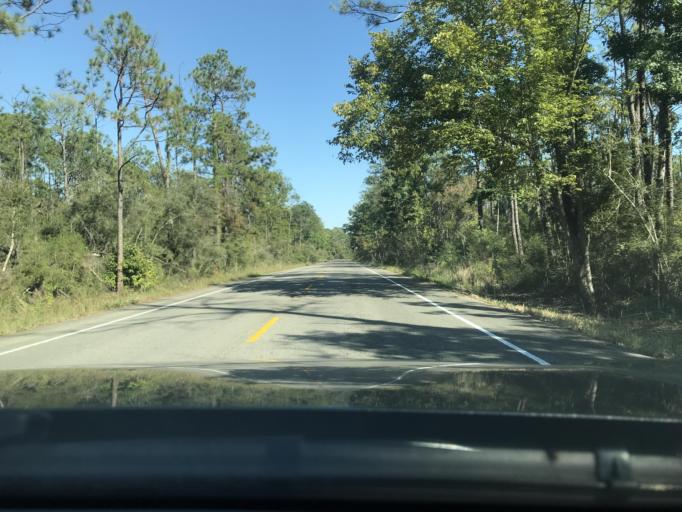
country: US
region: Louisiana
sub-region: Calcasieu Parish
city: Westlake
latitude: 30.3052
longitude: -93.2560
